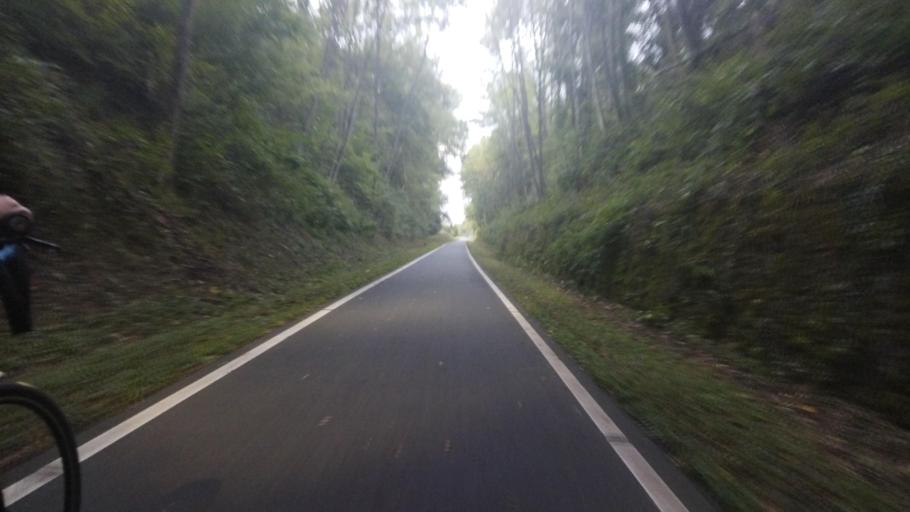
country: DE
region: North Rhine-Westphalia
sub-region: Regierungsbezirk Munster
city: Horstmar
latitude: 52.0603
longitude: 7.3204
